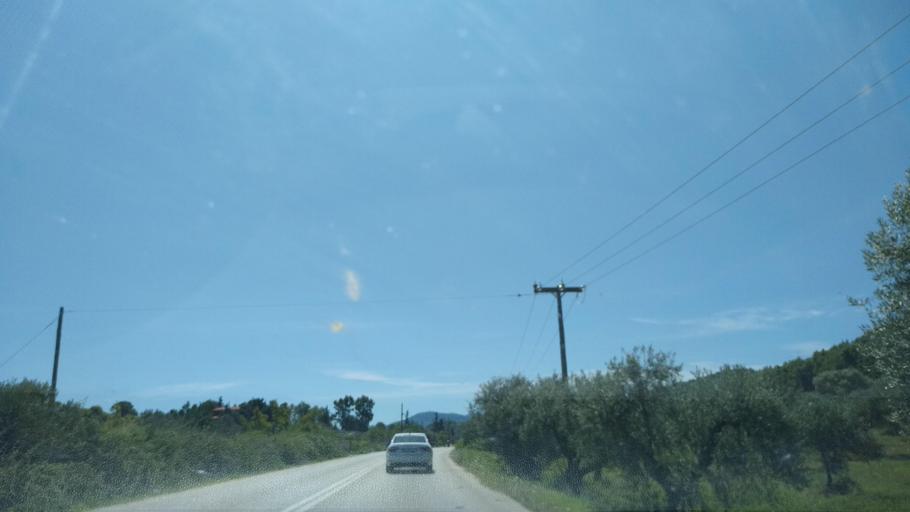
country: GR
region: Central Macedonia
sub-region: Nomos Chalkidikis
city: Agios Nikolaos
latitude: 40.2268
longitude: 23.7422
